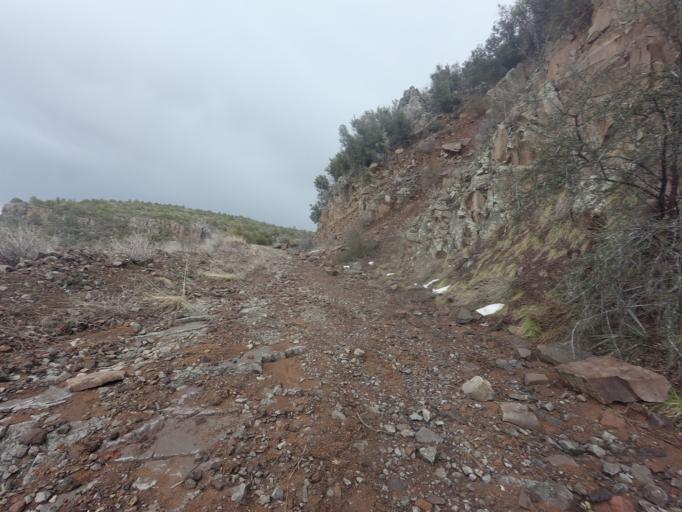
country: US
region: Arizona
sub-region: Gila County
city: Pine
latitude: 34.4083
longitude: -111.5793
